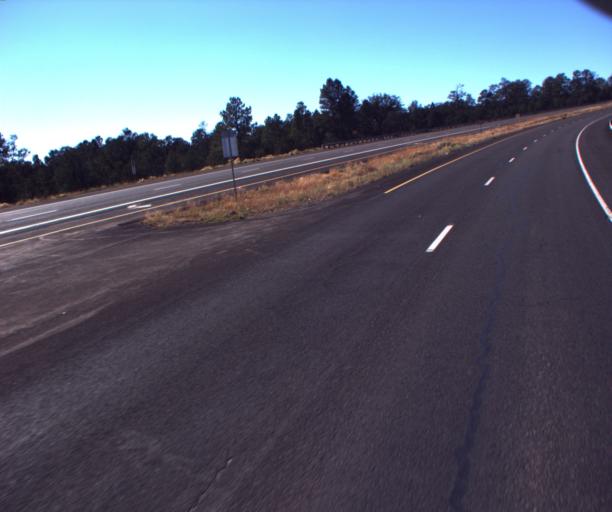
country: US
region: Arizona
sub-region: Apache County
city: Saint Michaels
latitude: 35.6563
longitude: -109.1505
